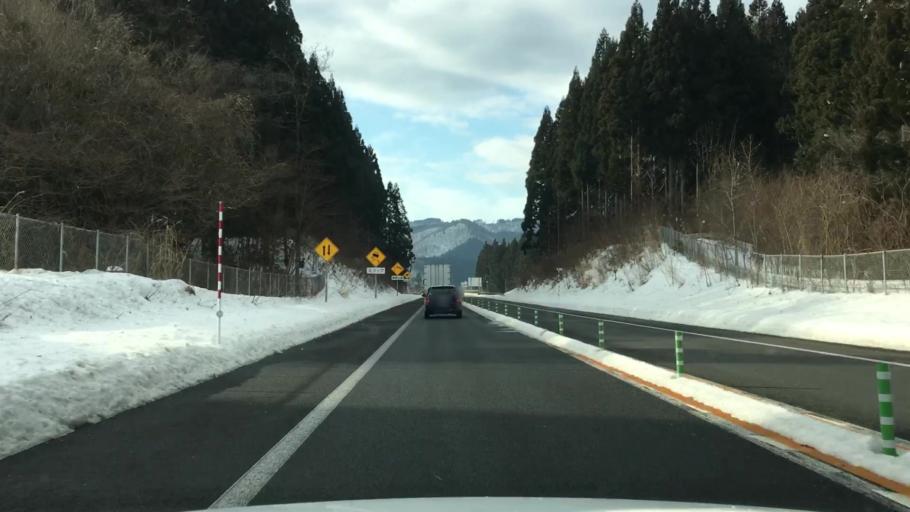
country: JP
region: Akita
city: Odate
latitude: 40.2436
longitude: 140.5091
